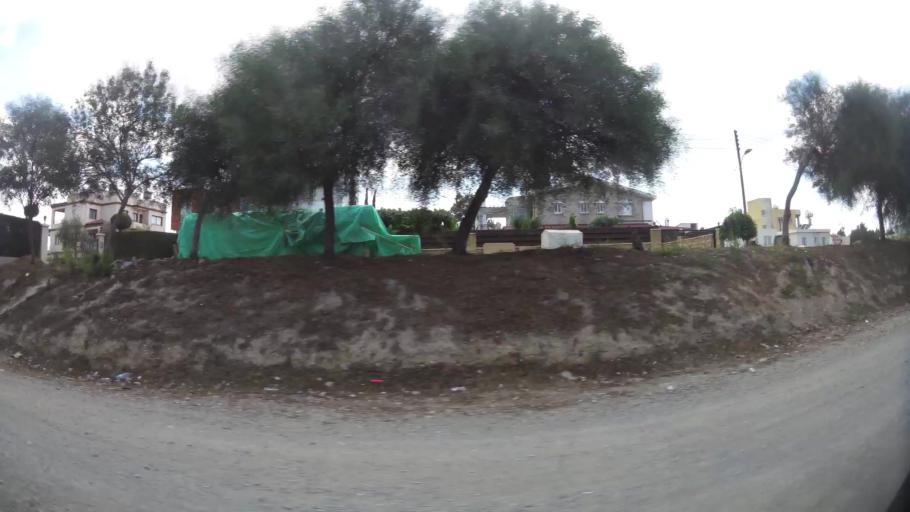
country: CY
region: Lefkosia
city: Nicosia
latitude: 35.2098
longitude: 33.3620
